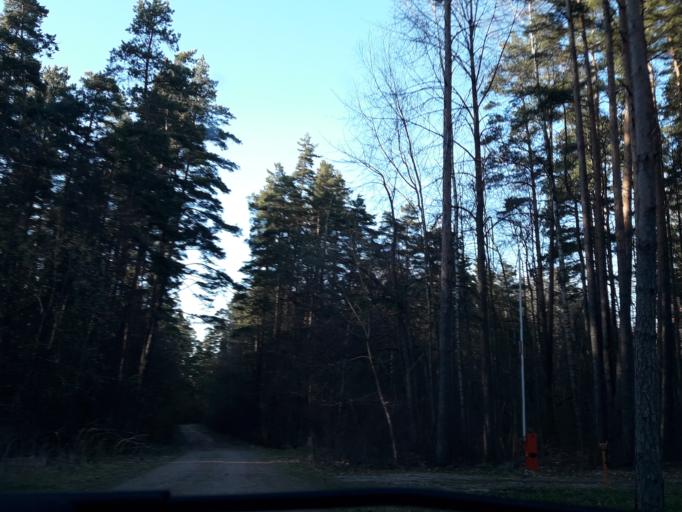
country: LV
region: Kekava
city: Kekava
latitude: 56.8548
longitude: 24.2321
